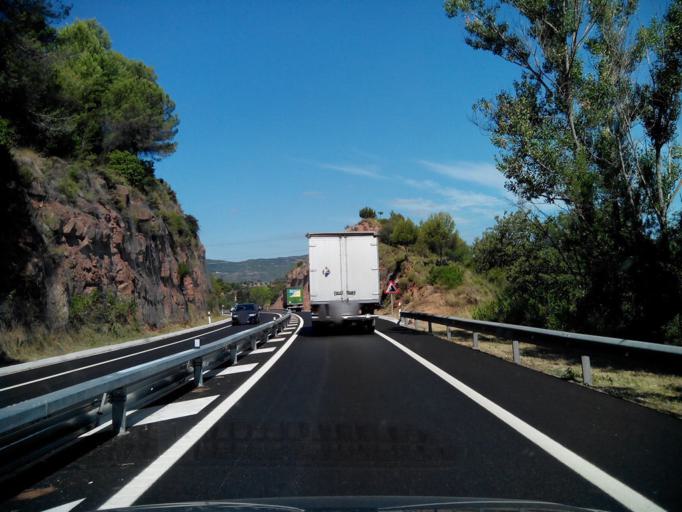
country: ES
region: Catalonia
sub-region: Provincia de Barcelona
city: Monistrol de Montserrat
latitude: 41.6018
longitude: 1.8894
